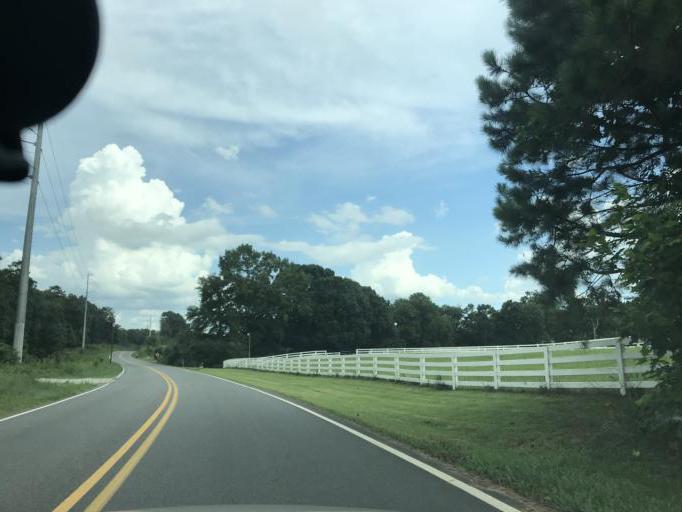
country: US
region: Georgia
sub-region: Cherokee County
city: Ball Ground
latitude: 34.3262
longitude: -84.2504
